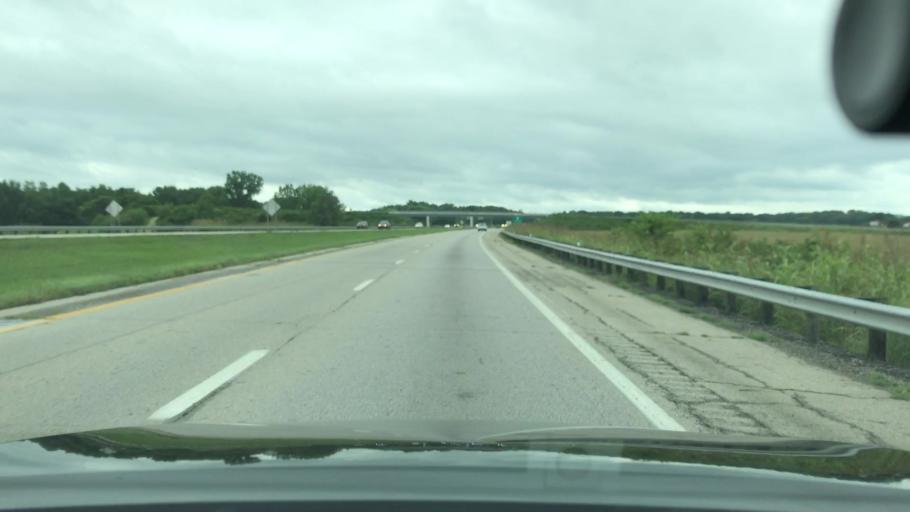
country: US
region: Ohio
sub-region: Ross County
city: Chillicothe
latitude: 39.3173
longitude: -82.9339
